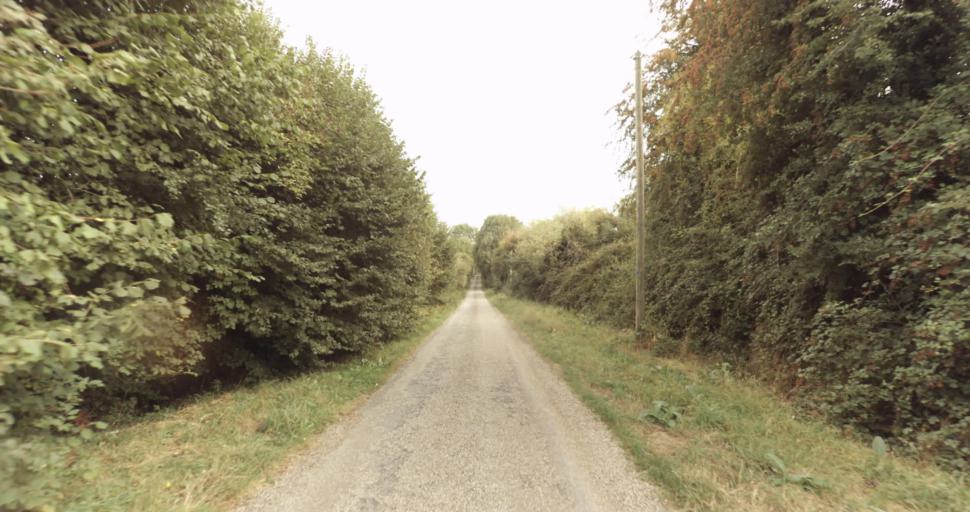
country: FR
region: Lower Normandy
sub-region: Departement de l'Orne
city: Vimoutiers
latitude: 48.9348
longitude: 0.2745
